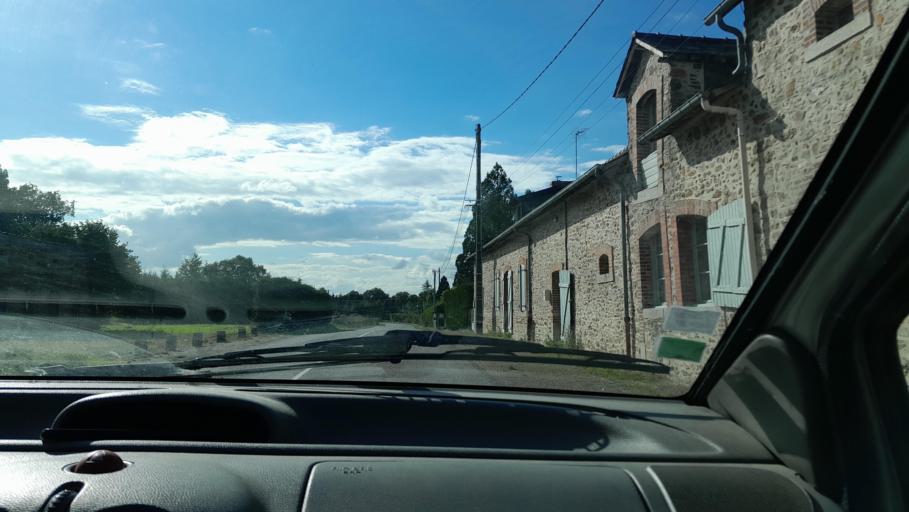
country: FR
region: Pays de la Loire
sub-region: Departement de la Mayenne
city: Ahuille
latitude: 48.0357
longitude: -0.8419
